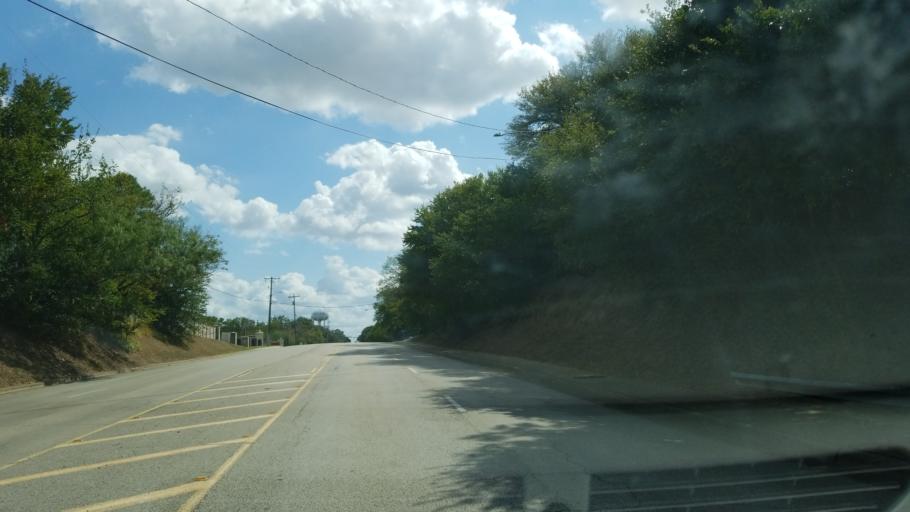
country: US
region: Texas
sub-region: Tarrant County
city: Euless
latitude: 32.8653
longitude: -97.0826
